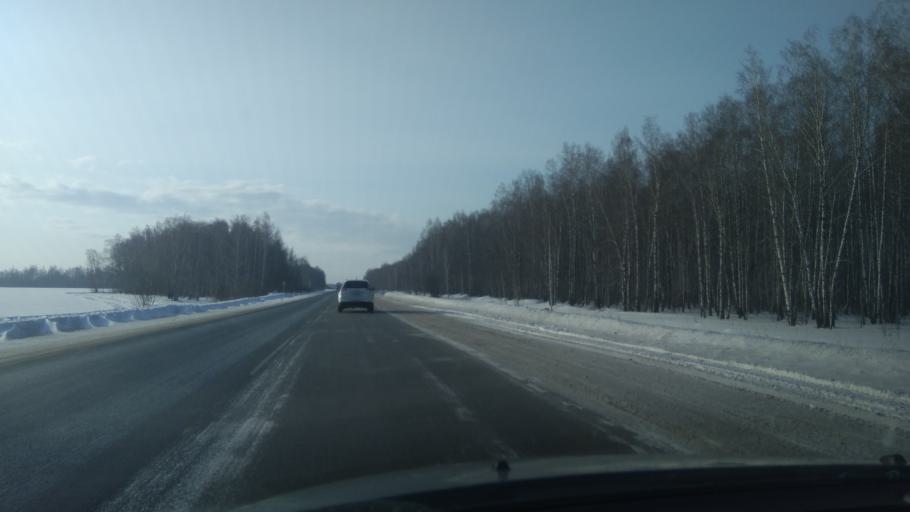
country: RU
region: Sverdlovsk
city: Bogdanovich
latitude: 56.8070
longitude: 62.0323
